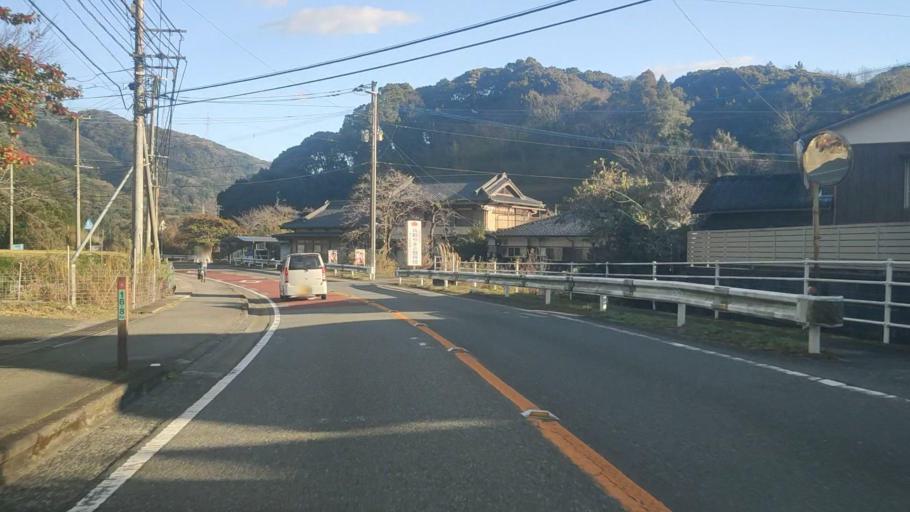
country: JP
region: Saga Prefecture
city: Saga-shi
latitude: 33.3431
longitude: 130.2489
